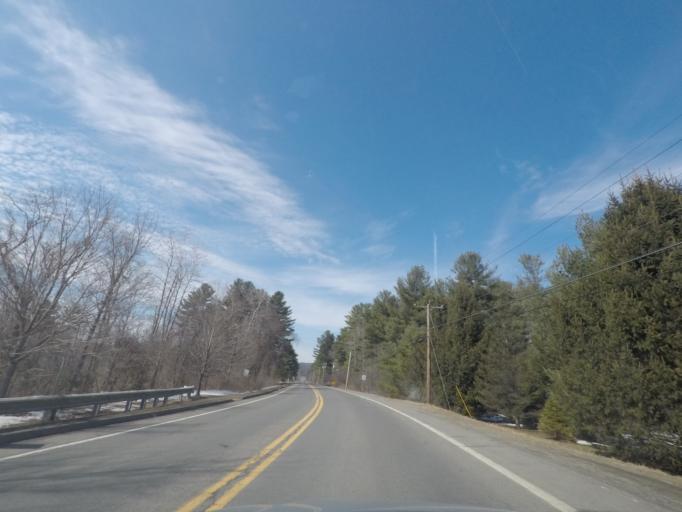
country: US
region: Massachusetts
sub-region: Berkshire County
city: Stockbridge
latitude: 42.2926
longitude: -73.3218
